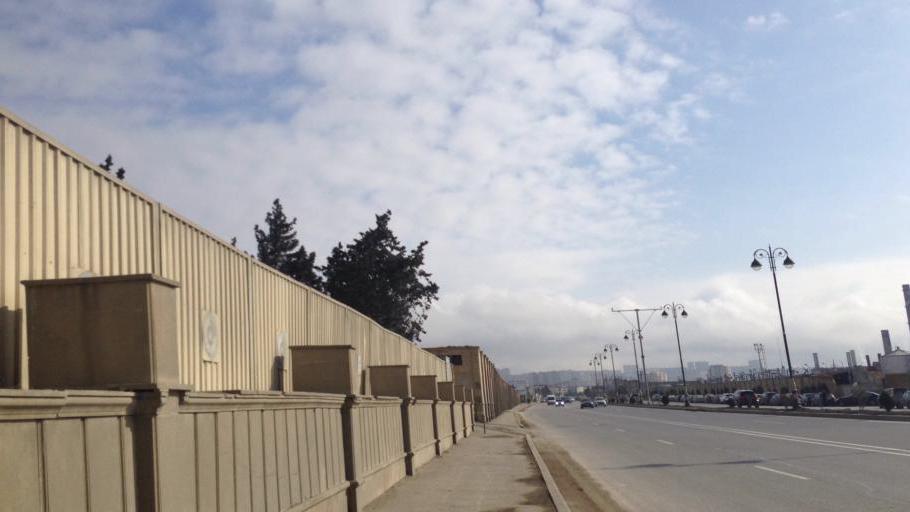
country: AZ
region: Baki
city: Baku
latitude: 40.3770
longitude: 49.9101
